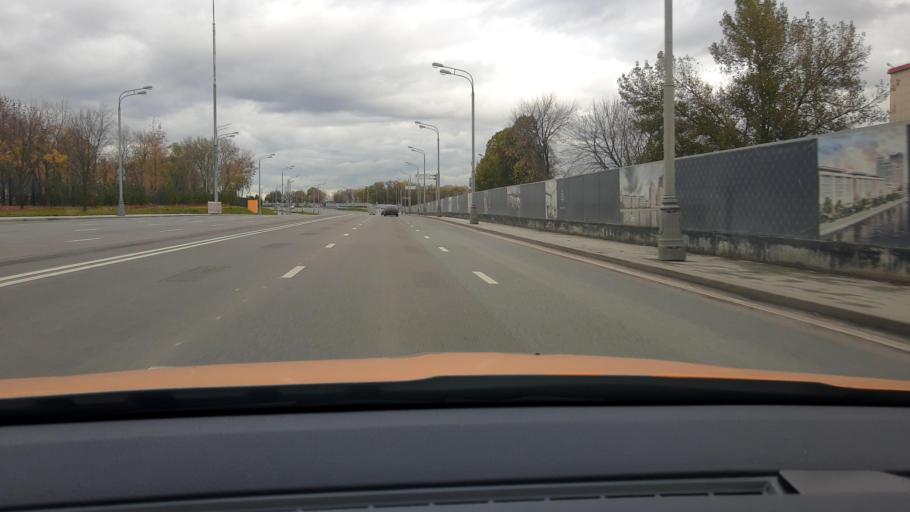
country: RU
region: Moskovskaya
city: Kozhukhovo
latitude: 55.6903
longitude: 37.6742
